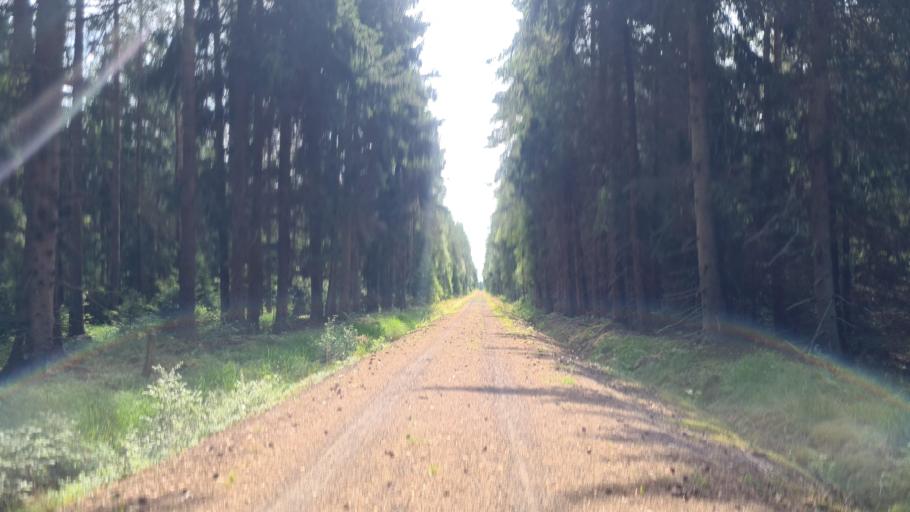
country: SE
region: Kronoberg
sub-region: Ljungby Kommun
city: Lagan
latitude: 56.9510
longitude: 13.9618
